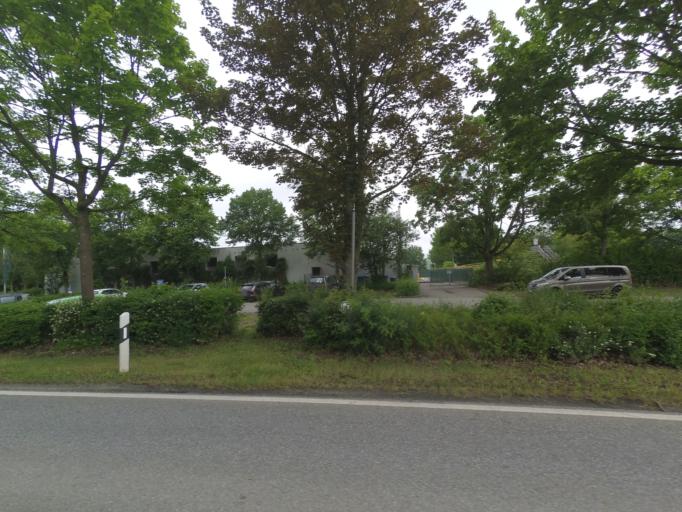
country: DE
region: Bavaria
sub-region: Lower Bavaria
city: Geiselhoring
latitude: 48.8319
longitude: 12.4035
